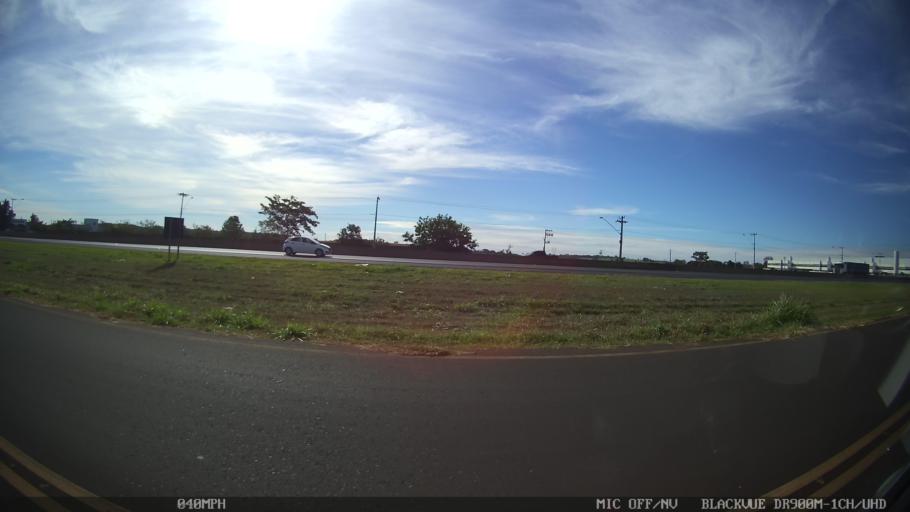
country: BR
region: Sao Paulo
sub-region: Sao Jose Do Rio Preto
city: Sao Jose do Rio Preto
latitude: -20.7943
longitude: -49.3103
